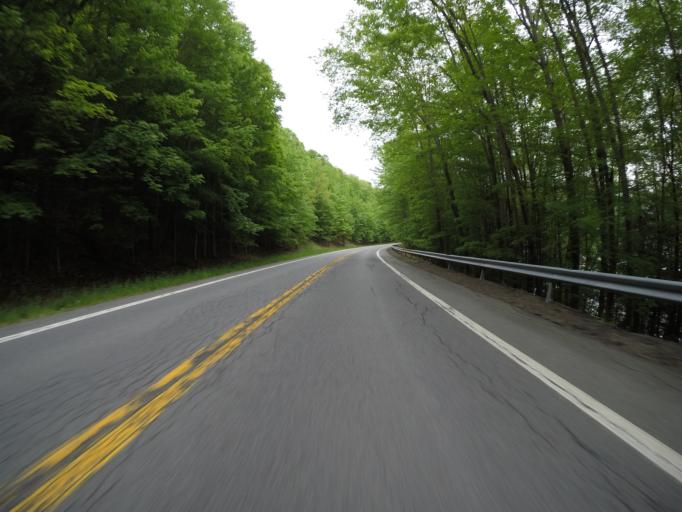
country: US
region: New York
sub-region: Sullivan County
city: Livingston Manor
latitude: 42.0808
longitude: -74.8792
